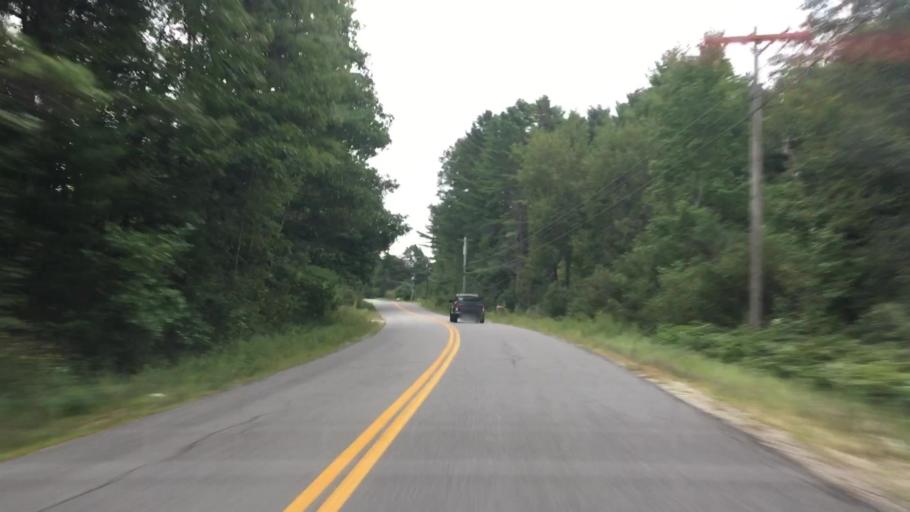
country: US
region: Maine
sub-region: Cumberland County
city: Freeport
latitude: 43.8857
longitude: -70.1703
